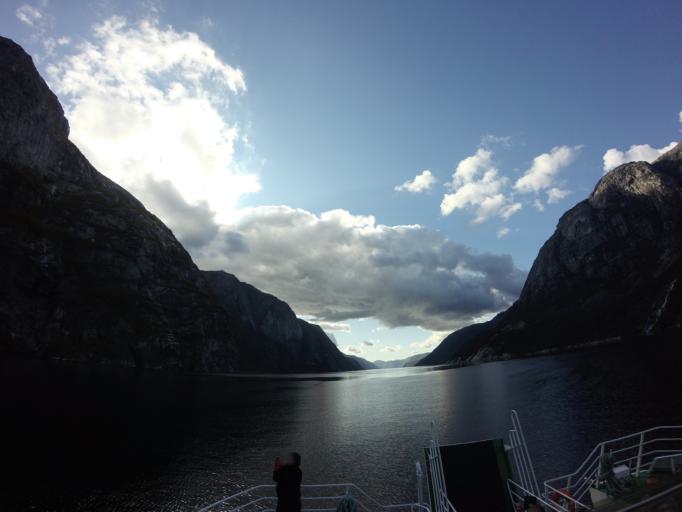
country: NO
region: Vest-Agder
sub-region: Sirdal
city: Tonstad
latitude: 59.0399
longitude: 6.5624
